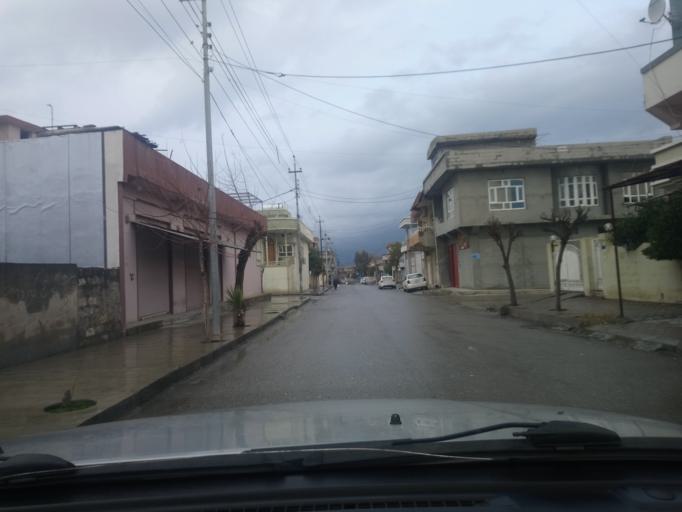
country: IQ
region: As Sulaymaniyah
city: Qeladize
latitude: 36.1874
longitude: 45.1261
